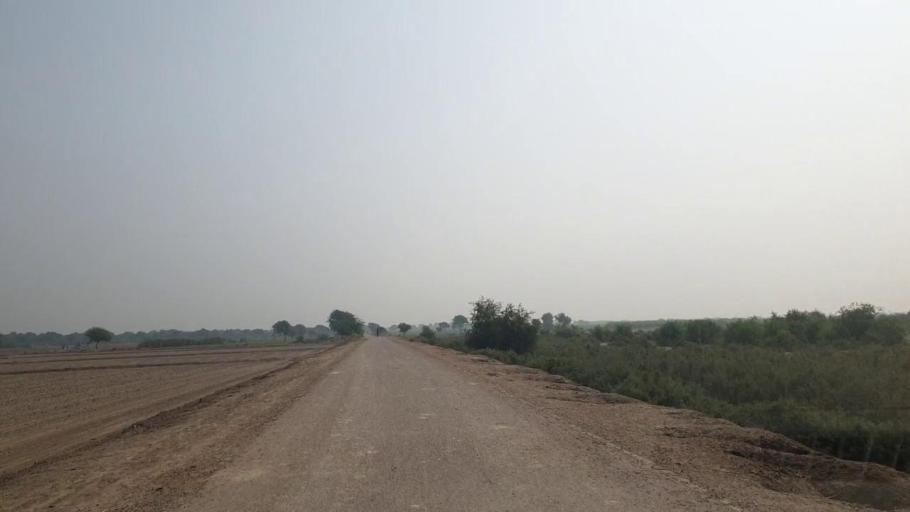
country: PK
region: Sindh
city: Tando Muhammad Khan
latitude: 25.2479
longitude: 68.5561
